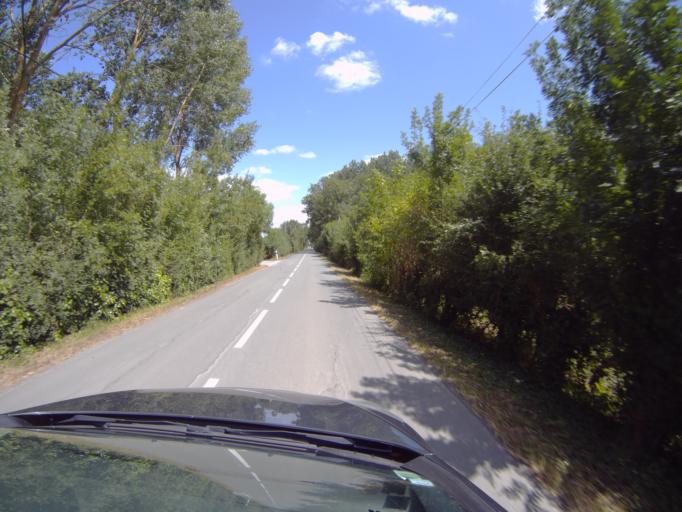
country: FR
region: Poitou-Charentes
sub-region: Departement des Deux-Sevres
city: Saint-Hilaire-la-Palud
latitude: 46.2532
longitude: -0.7523
